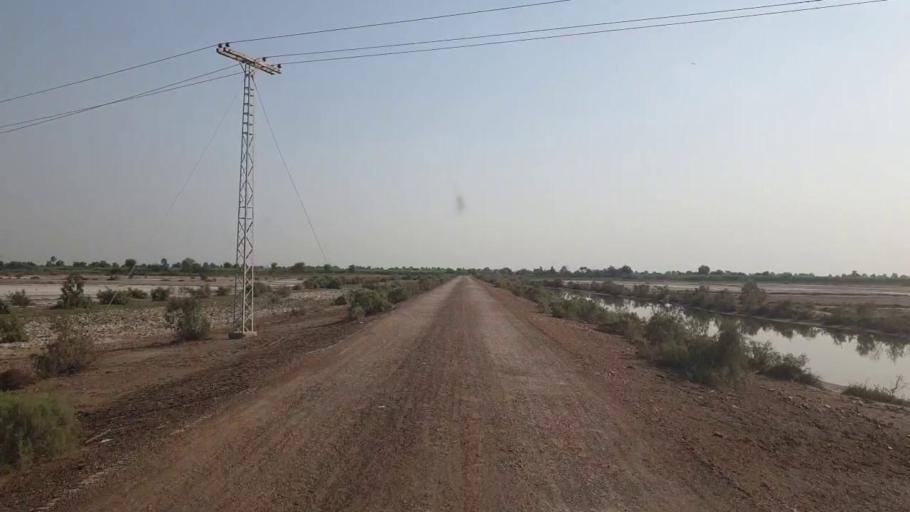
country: PK
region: Sindh
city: Sanghar
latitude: 26.0486
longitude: 68.8973
